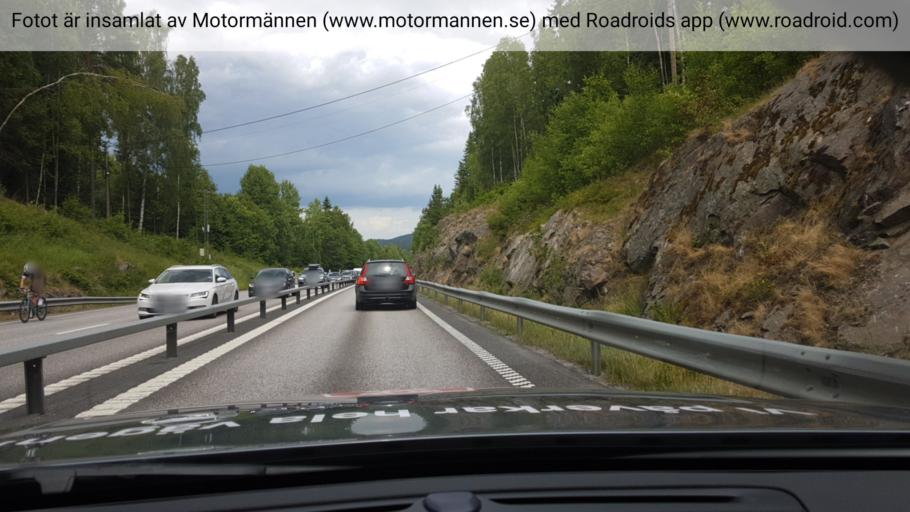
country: SE
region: OEstergoetland
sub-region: Motala Kommun
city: Ryd
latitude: 58.7689
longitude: 14.9928
